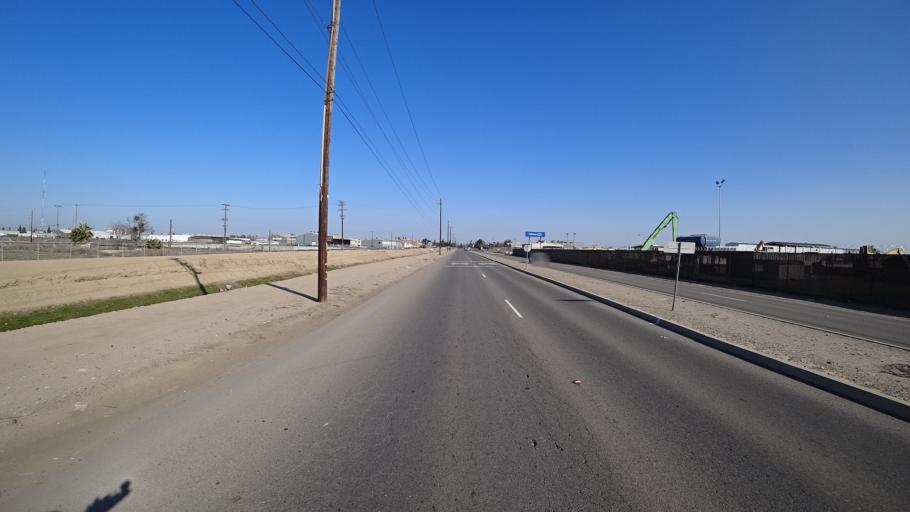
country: US
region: California
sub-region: Fresno County
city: Fresno
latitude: 36.7009
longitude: -119.7366
